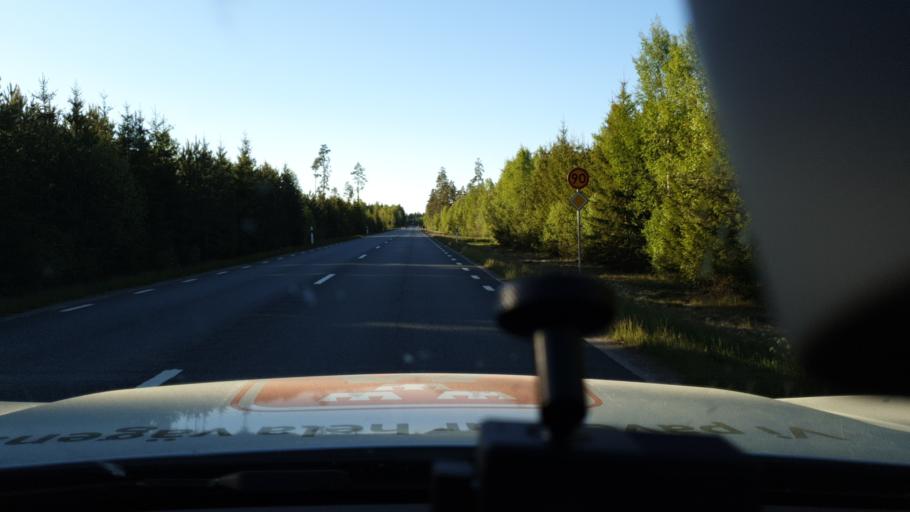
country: SE
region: Joenkoeping
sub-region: Eksjo Kommun
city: Eksjoe
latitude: 57.6248
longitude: 14.9705
